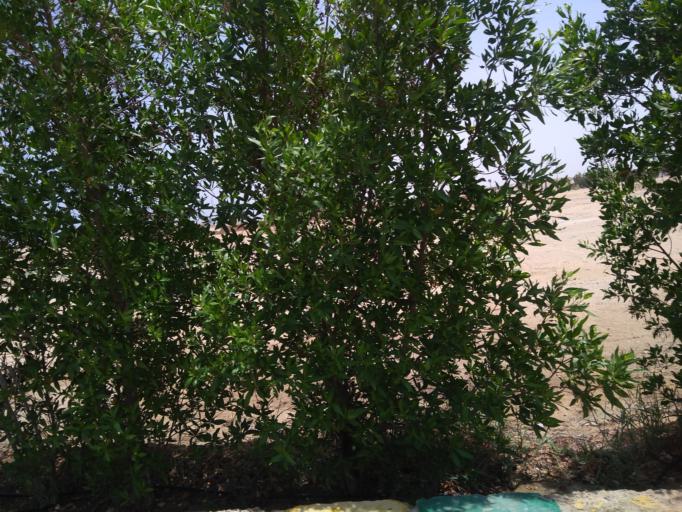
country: EG
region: Red Sea
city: Al Qusayr
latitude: 25.9123
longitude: 34.4043
